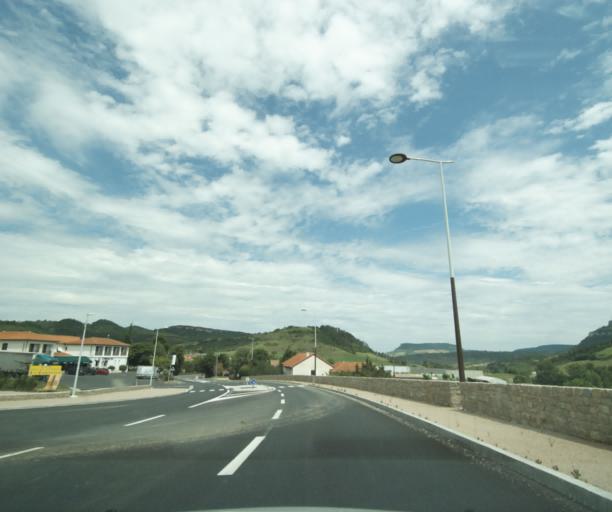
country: FR
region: Midi-Pyrenees
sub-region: Departement de l'Aveyron
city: Saint-Affrique
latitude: 43.9721
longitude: 2.9618
